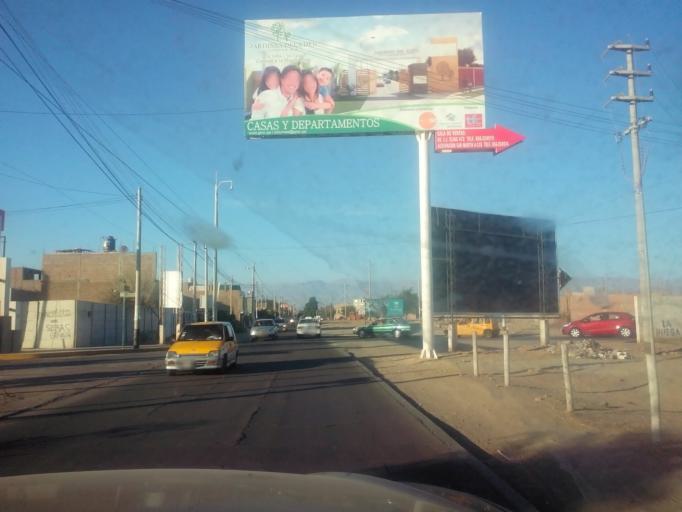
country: PE
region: Ica
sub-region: Provincia de Ica
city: Ica
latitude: -14.0814
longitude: -75.7498
